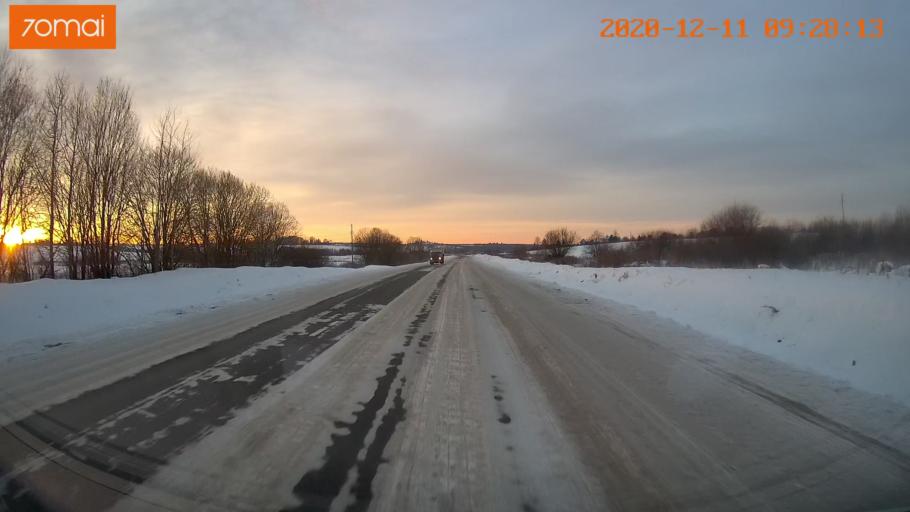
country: RU
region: Vologda
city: Vologda
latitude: 59.1556
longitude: 40.0094
